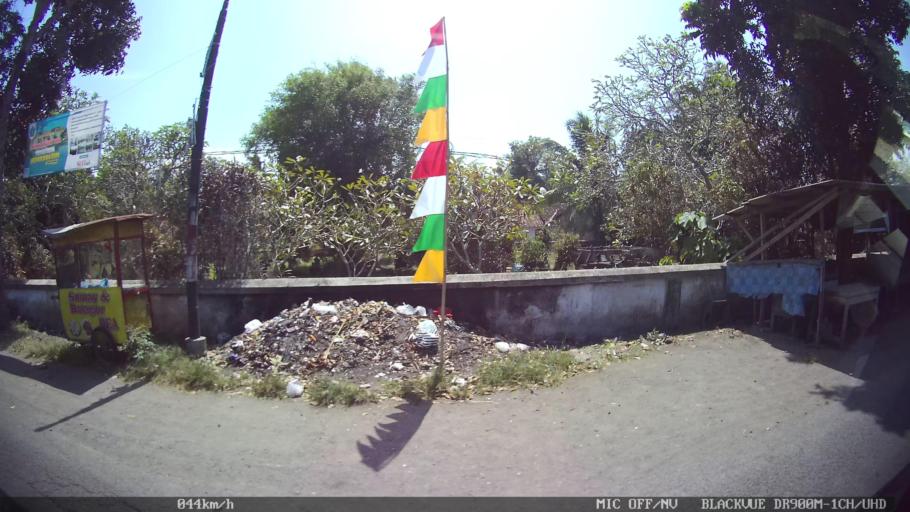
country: ID
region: Daerah Istimewa Yogyakarta
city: Srandakan
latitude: -7.9073
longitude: 110.0823
